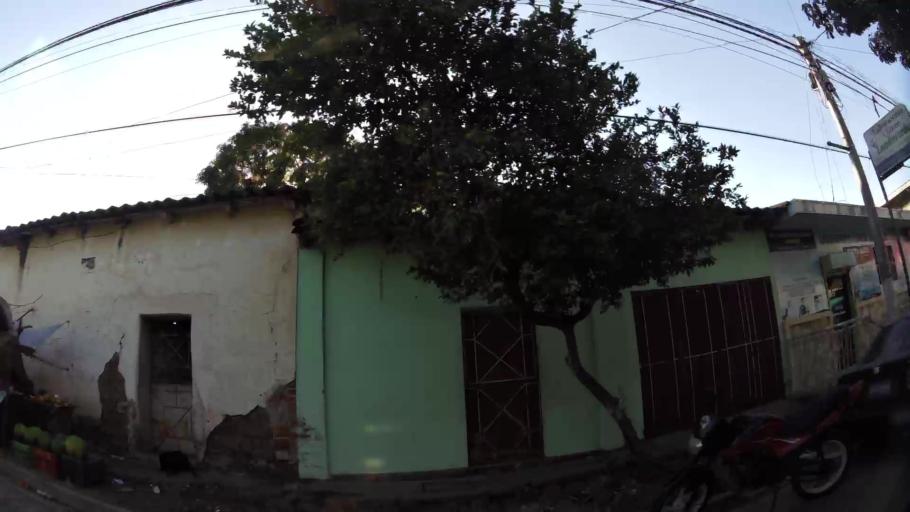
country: SV
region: Santa Ana
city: Metapan
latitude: 14.3277
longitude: -89.4459
